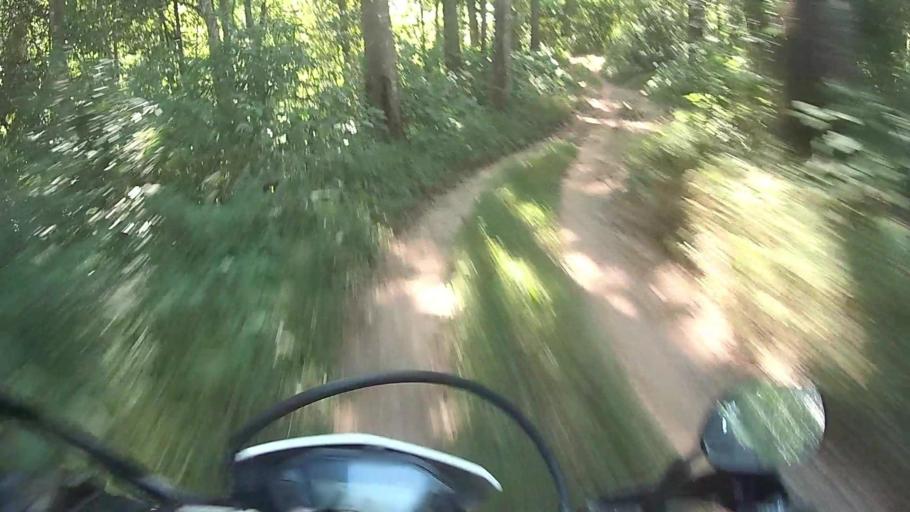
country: TH
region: Chiang Mai
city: Samoeng
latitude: 18.9805
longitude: 98.8096
